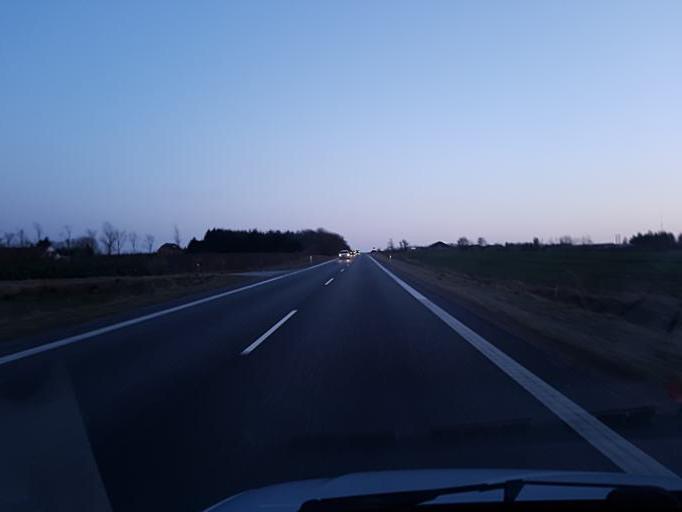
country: DK
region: Central Jutland
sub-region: Ringkobing-Skjern Kommune
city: Videbaek
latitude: 56.2058
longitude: 8.5817
